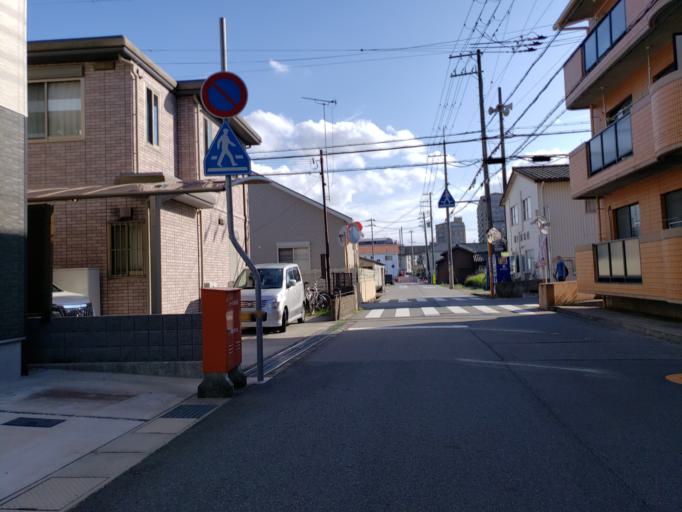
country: JP
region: Hyogo
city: Kakogawacho-honmachi
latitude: 34.7627
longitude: 134.8487
